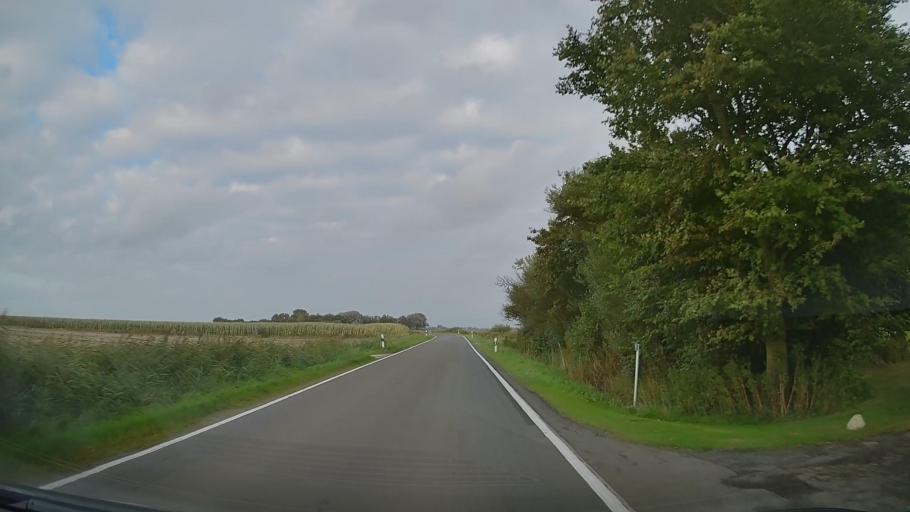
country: DE
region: Schleswig-Holstein
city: Osterhever
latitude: 54.3966
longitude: 8.7615
